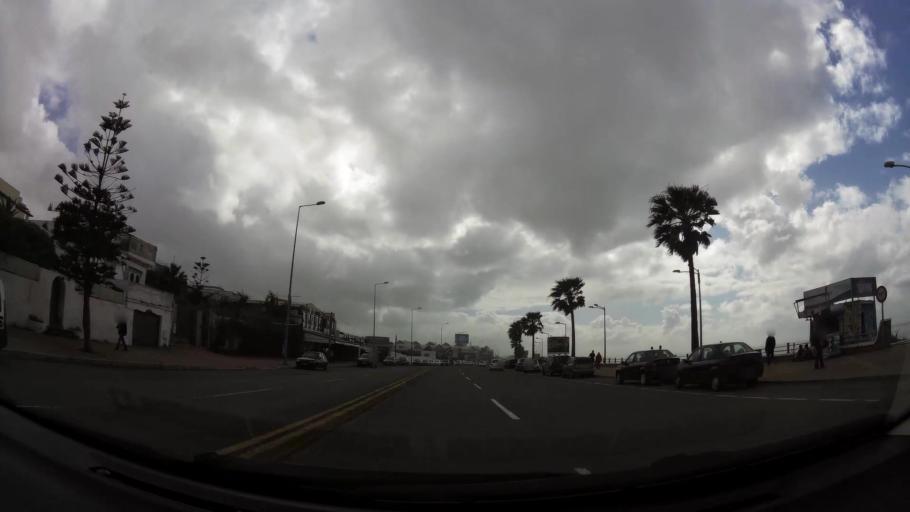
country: MA
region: Grand Casablanca
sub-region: Casablanca
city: Casablanca
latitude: 33.5900
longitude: -7.6796
